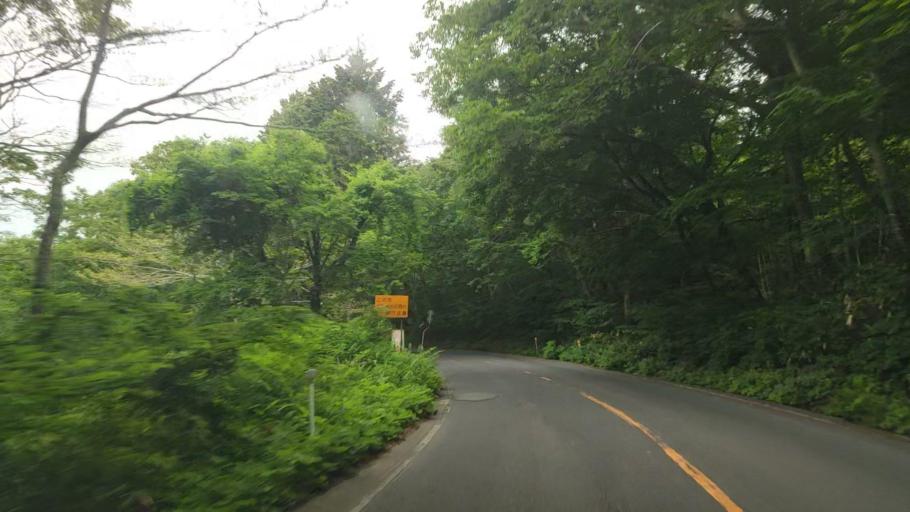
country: JP
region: Tottori
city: Yonago
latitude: 35.3570
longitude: 133.5329
